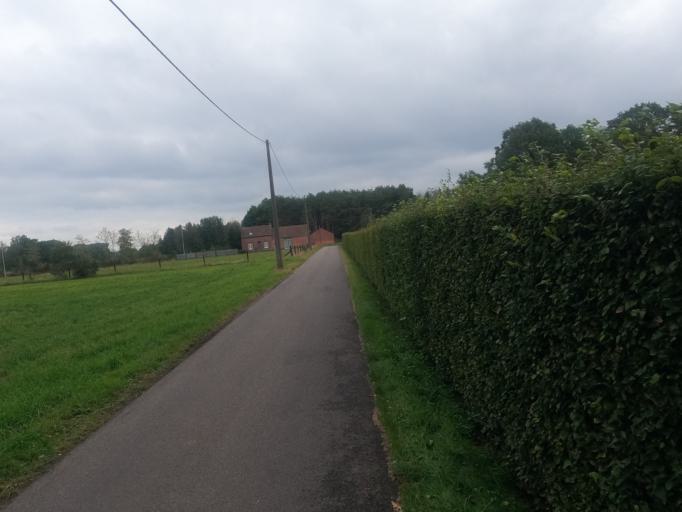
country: BE
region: Flanders
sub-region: Provincie Antwerpen
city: Nijlen
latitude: 51.1436
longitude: 4.6613
